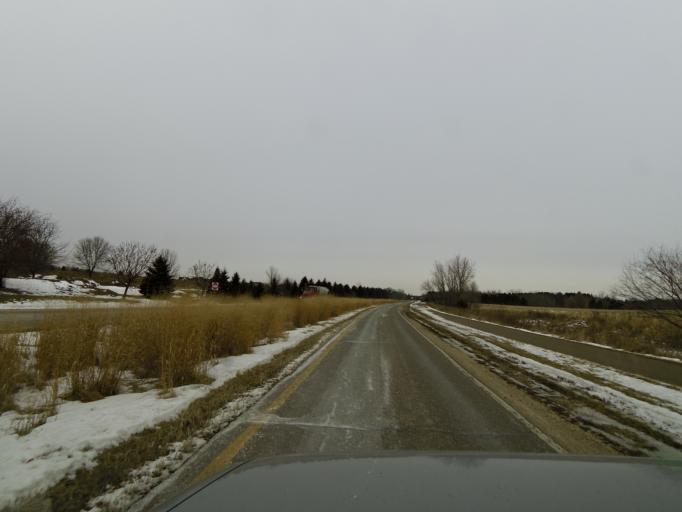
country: US
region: Minnesota
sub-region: Washington County
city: Lake Elmo
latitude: 44.9644
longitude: -92.9033
